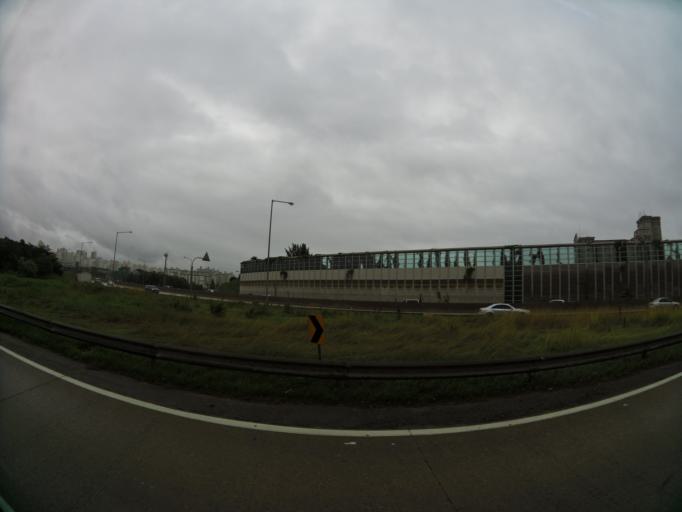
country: KR
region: Gyeonggi-do
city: Suwon-si
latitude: 37.2902
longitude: 127.1000
